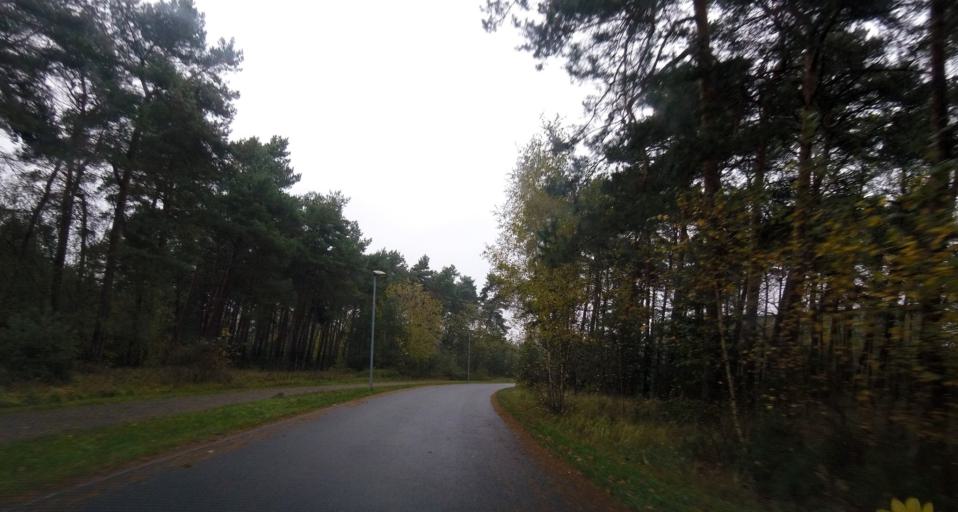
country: DE
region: Brandenburg
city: Niedergorsdorf
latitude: 52.0013
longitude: 12.9915
